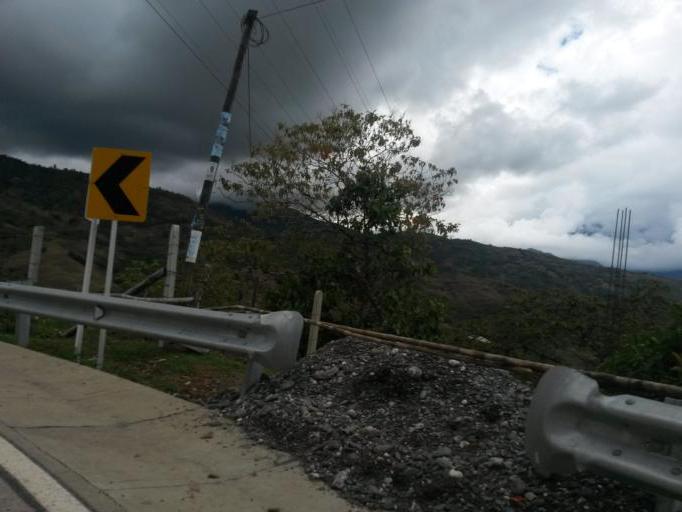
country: CO
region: Cauca
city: Almaguer
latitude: 1.8321
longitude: -76.9708
